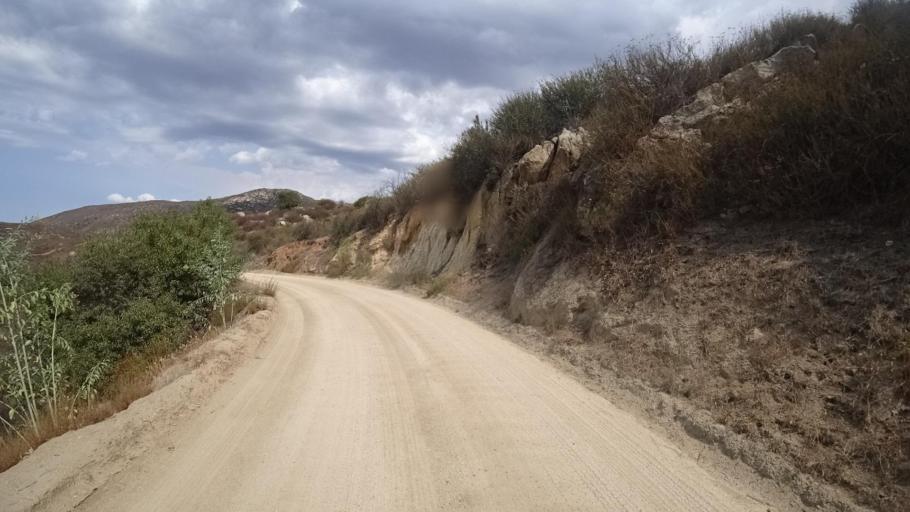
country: US
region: California
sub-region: San Diego County
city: Ramona
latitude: 33.1009
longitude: -116.8260
